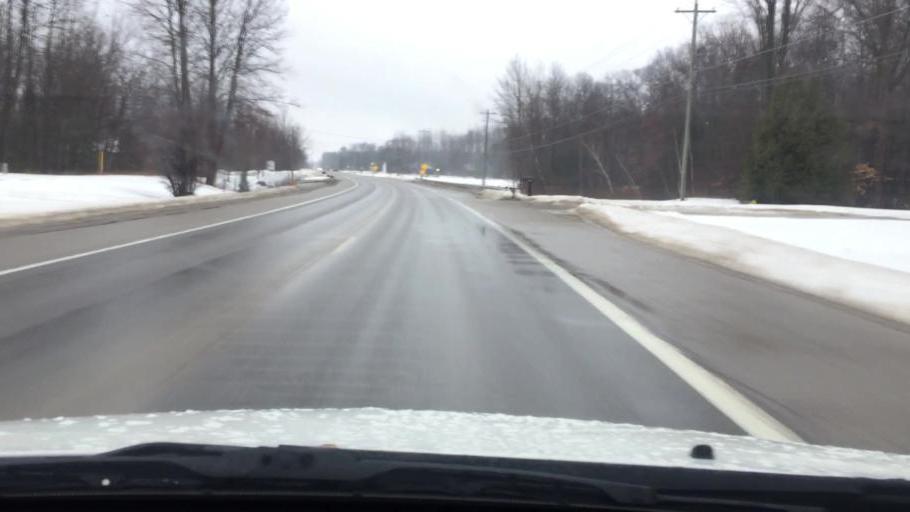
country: US
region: Michigan
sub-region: Charlevoix County
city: Charlevoix
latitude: 45.2964
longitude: -85.2543
